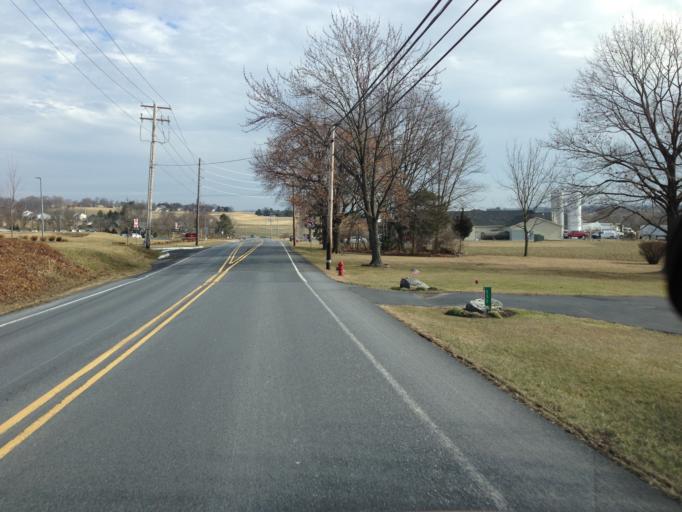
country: US
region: Pennsylvania
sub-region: Lancaster County
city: Manheim
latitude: 40.1733
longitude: -76.3745
